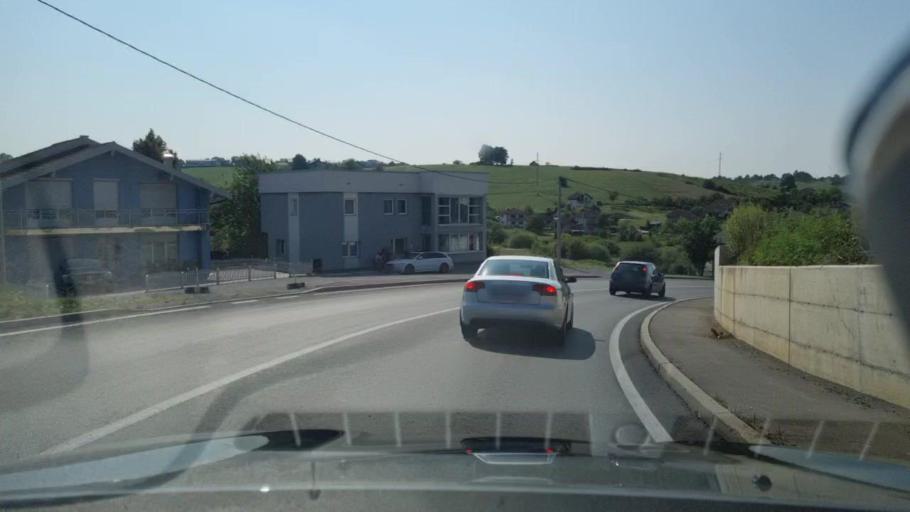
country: BA
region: Federation of Bosnia and Herzegovina
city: Cazin
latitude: 44.9681
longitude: 15.9002
